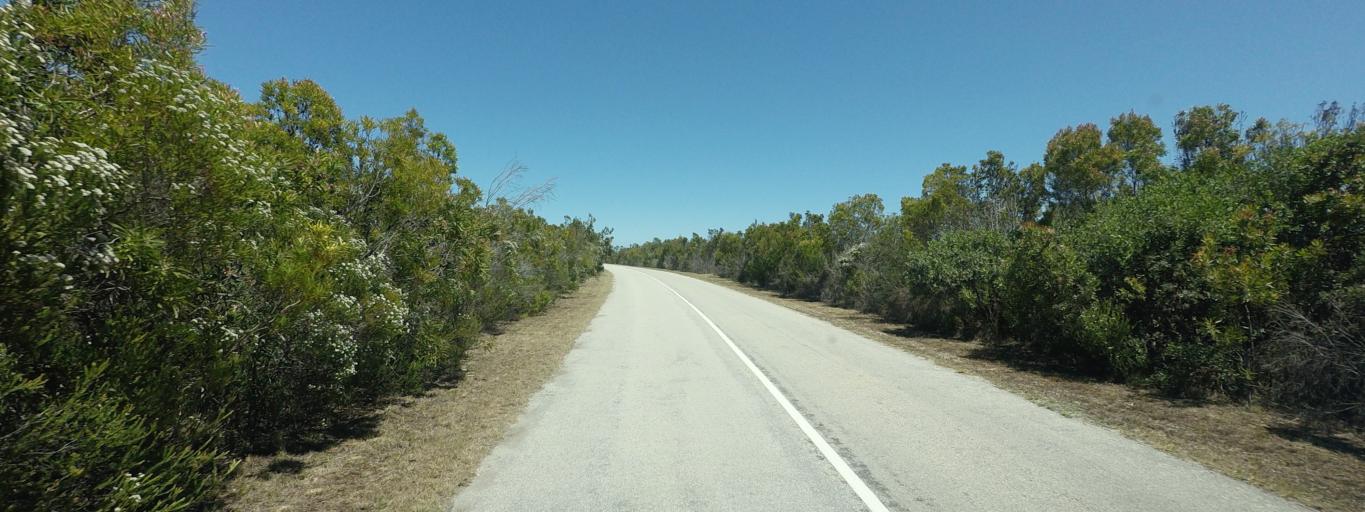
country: ZA
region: Western Cape
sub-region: Eden District Municipality
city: Plettenberg Bay
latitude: -33.9601
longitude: 23.5355
